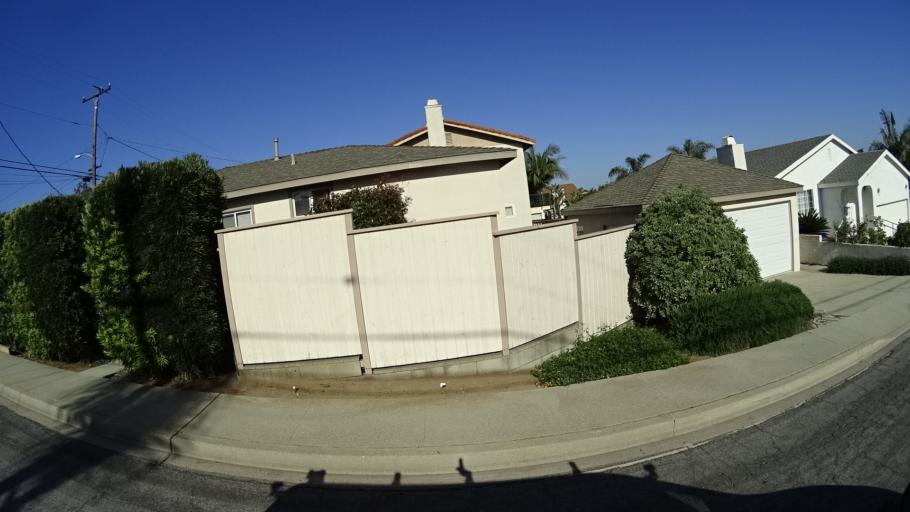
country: US
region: California
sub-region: Los Angeles County
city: Redondo Beach
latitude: 33.8635
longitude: -118.3707
